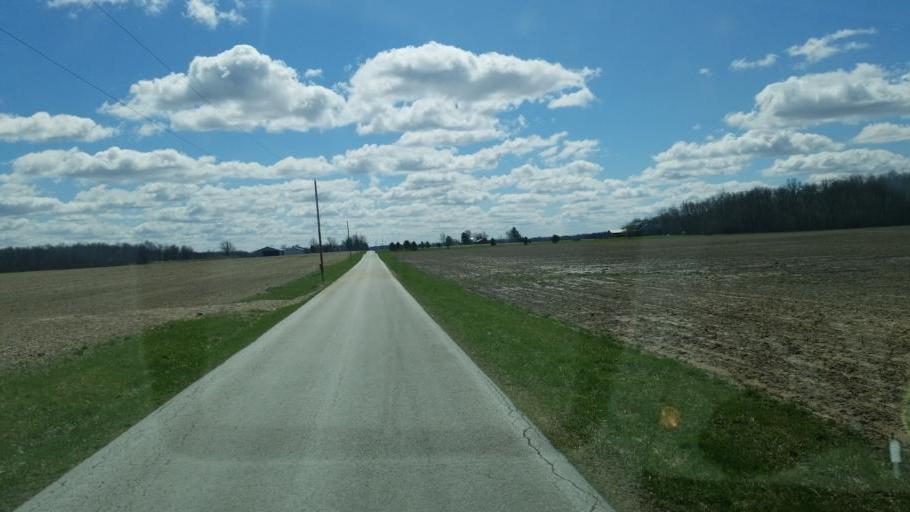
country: US
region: Ohio
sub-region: Hancock County
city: Arlington
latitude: 40.9266
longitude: -83.5369
